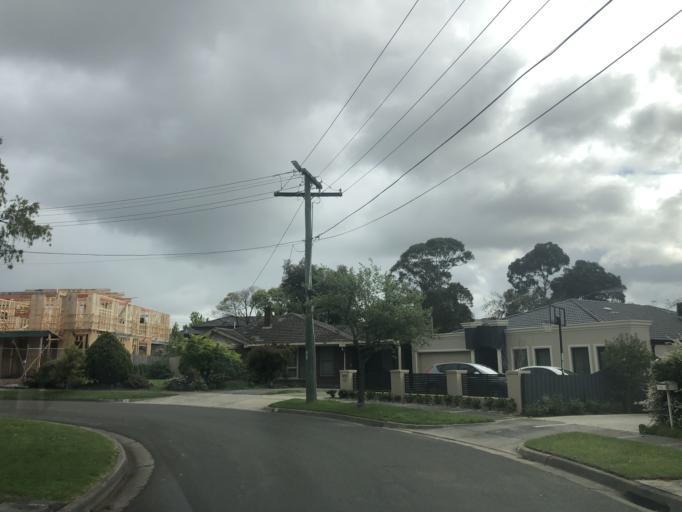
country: AU
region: Victoria
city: Burwood East
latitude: -37.8672
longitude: 145.1460
